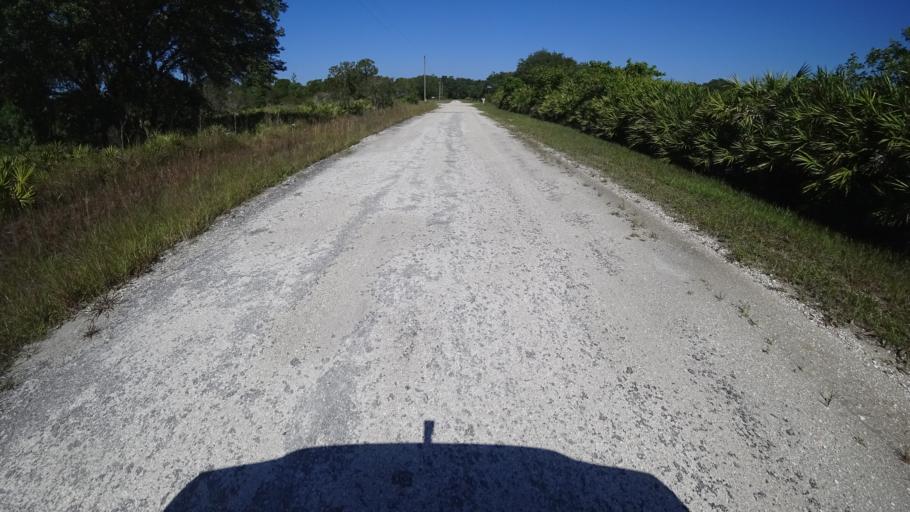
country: US
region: Florida
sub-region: Sarasota County
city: The Meadows
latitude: 27.4090
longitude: -82.2989
